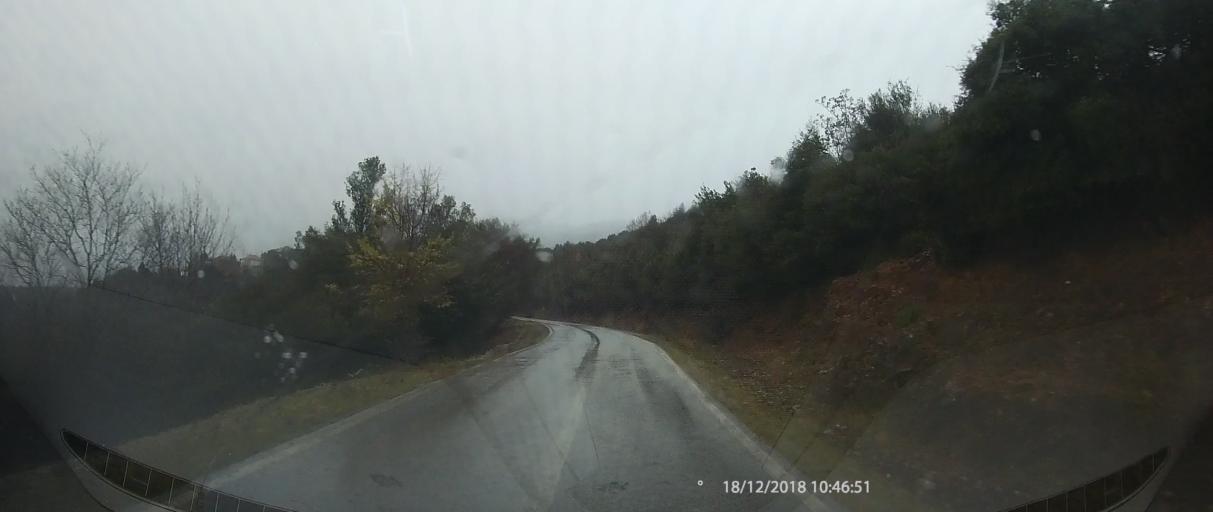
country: GR
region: Central Macedonia
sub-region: Nomos Pierias
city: Kato Milia
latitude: 40.1848
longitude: 22.3260
